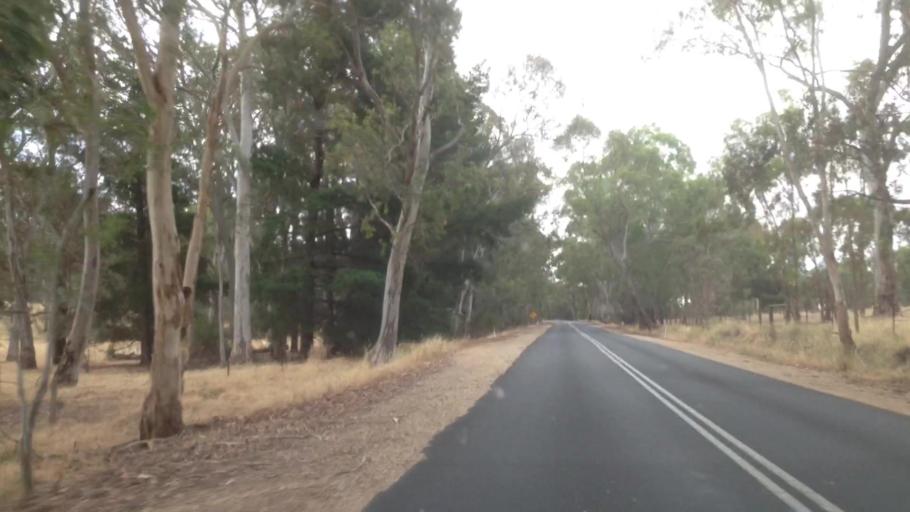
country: AU
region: South Australia
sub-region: Barossa
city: Williamstown
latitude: -34.6495
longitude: 138.8630
